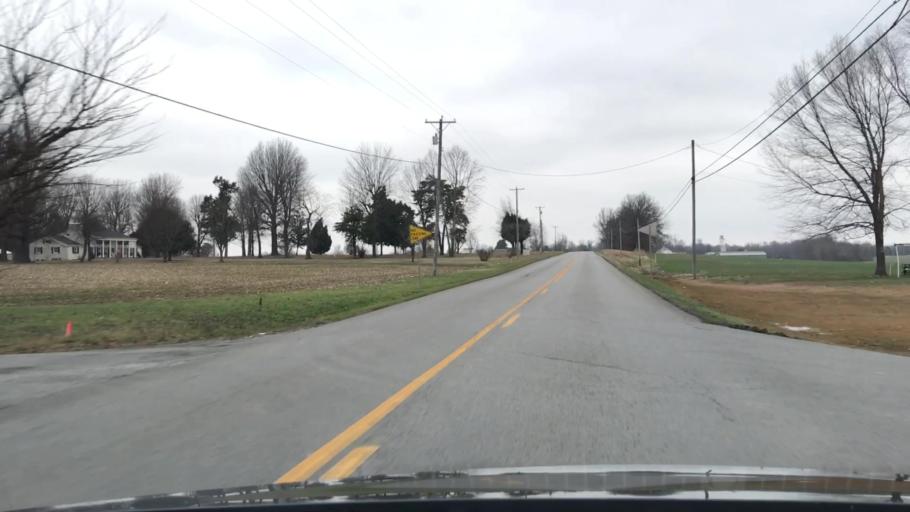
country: US
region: Kentucky
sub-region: Muhlenberg County
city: Morehead
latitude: 37.3921
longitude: -87.2553
